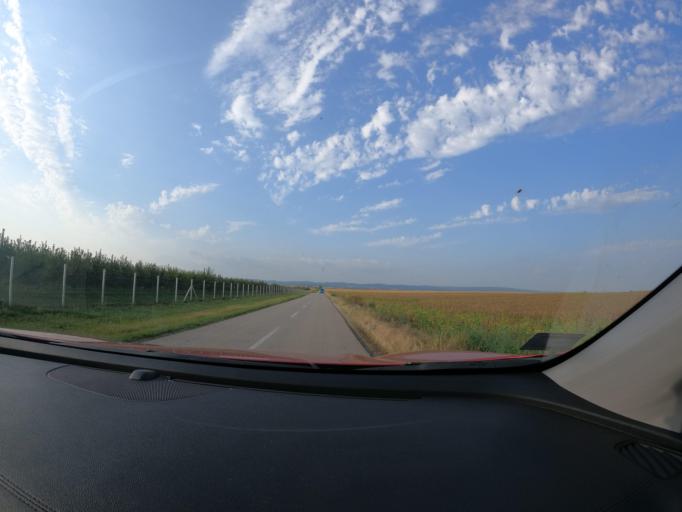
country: RS
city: Vrdnik
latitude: 45.0657
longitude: 19.8087
